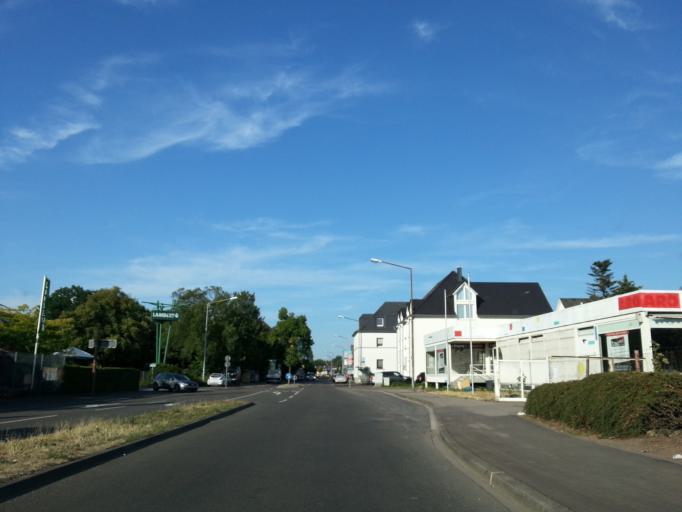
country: DE
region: Rheinland-Pfalz
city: Trier
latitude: 49.7638
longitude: 6.6576
